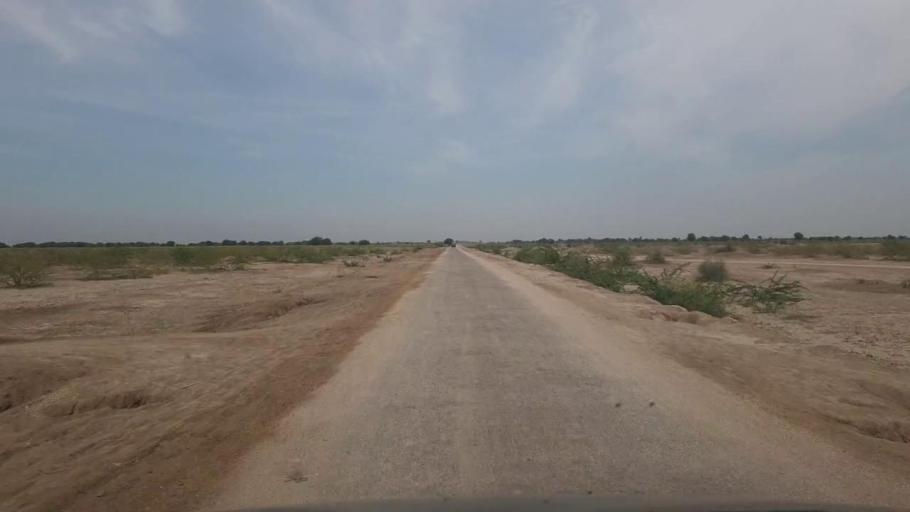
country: PK
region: Sindh
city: Kunri
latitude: 25.2424
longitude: 69.6158
